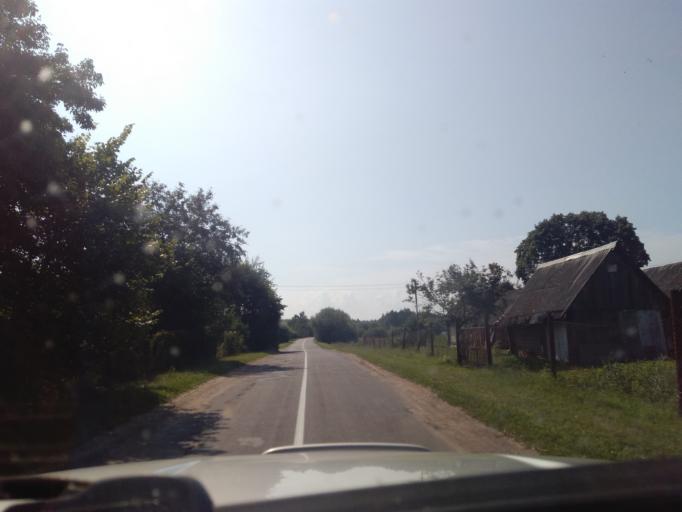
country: BY
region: Minsk
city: Valozhyn
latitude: 54.0170
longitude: 26.6039
